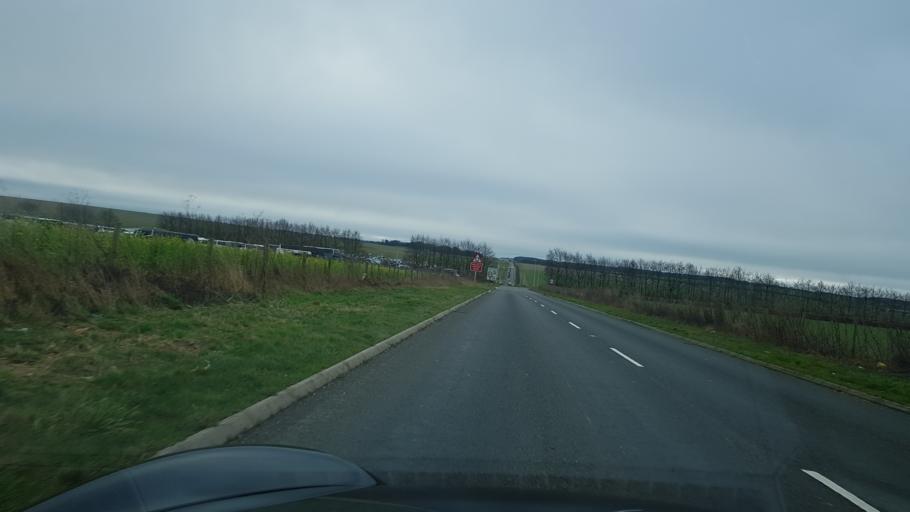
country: GB
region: England
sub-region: Wiltshire
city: Shrewton
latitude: 51.1877
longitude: -1.8609
